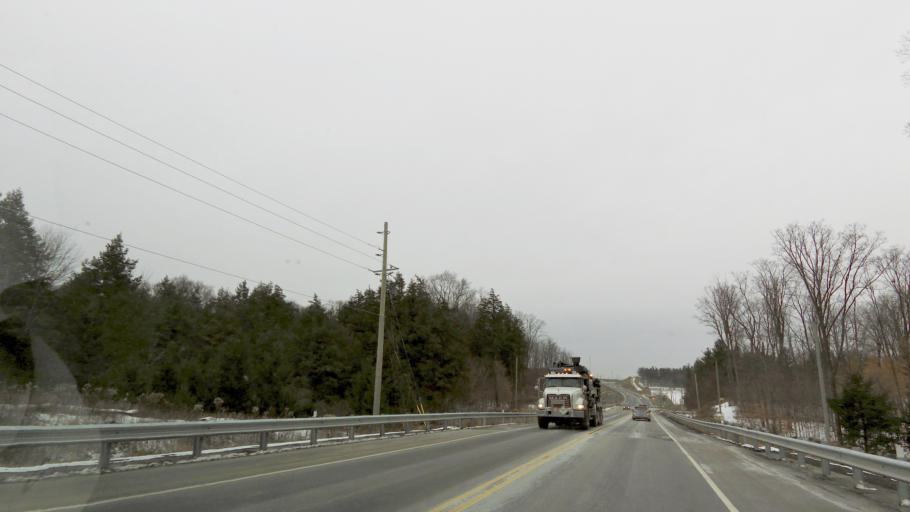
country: CA
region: Ontario
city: Newmarket
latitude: 44.0705
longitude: -79.5116
